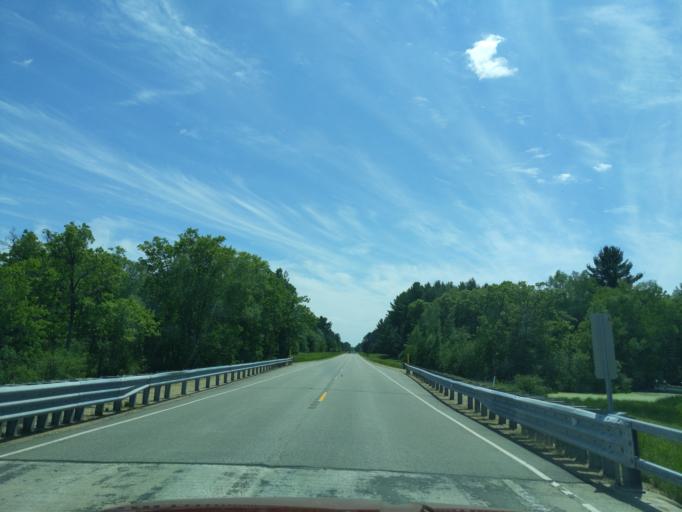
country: US
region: Wisconsin
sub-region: Marquette County
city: Montello
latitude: 43.9159
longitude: -89.3122
